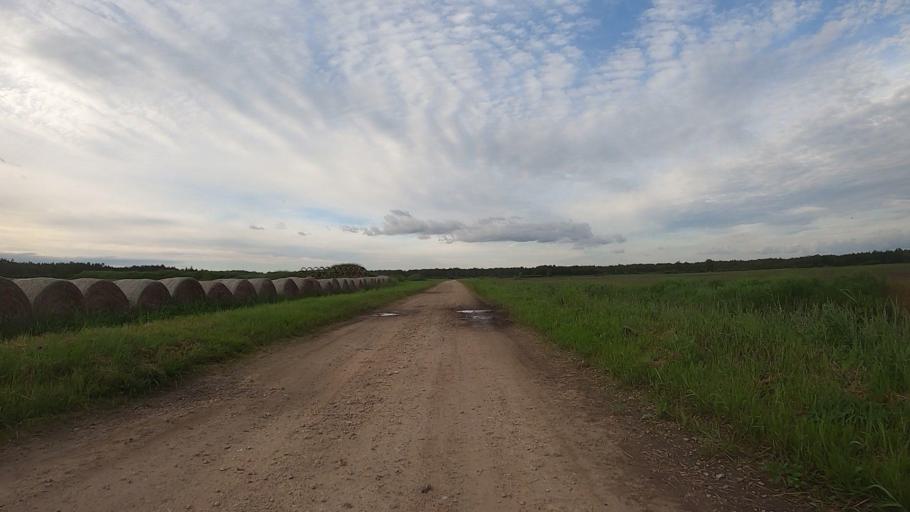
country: LV
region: Olaine
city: Olaine
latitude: 56.8232
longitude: 23.9548
